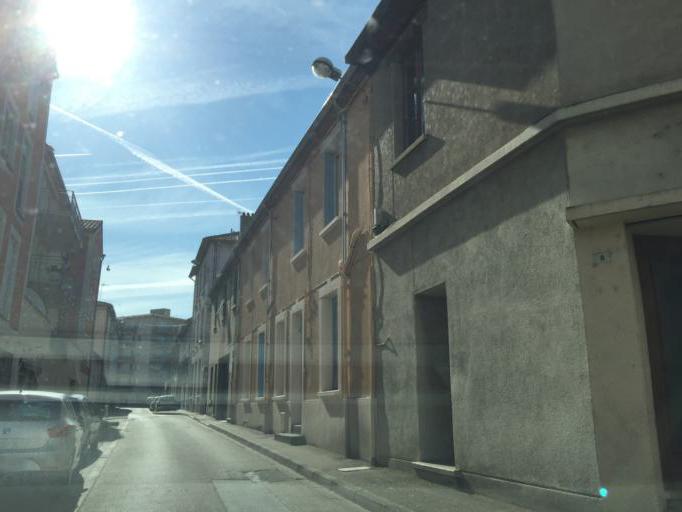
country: FR
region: Rhone-Alpes
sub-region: Departement de la Loire
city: Feurs
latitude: 45.7429
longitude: 4.2220
